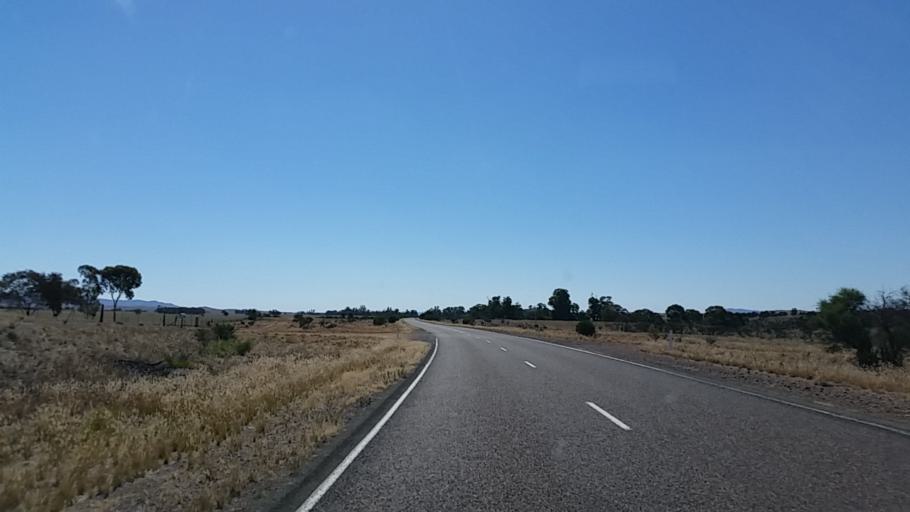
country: AU
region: South Australia
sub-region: Flinders Ranges
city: Quorn
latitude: -32.4892
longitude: 138.5461
